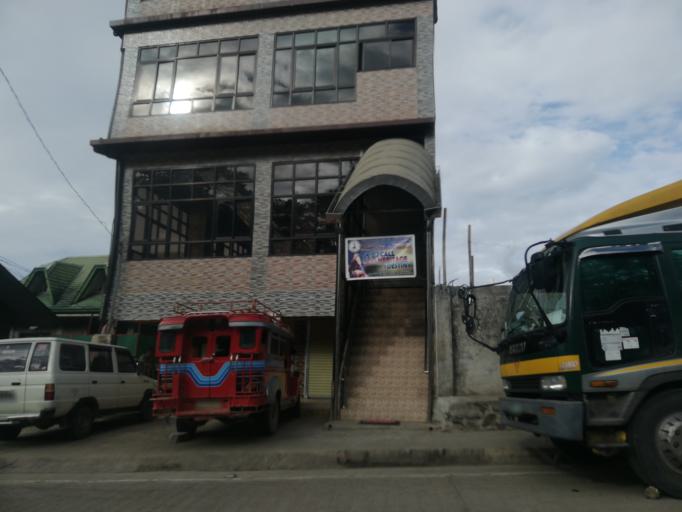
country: PH
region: Cordillera
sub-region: Province of Benguet
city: La Trinidad
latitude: 16.4448
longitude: 120.5804
